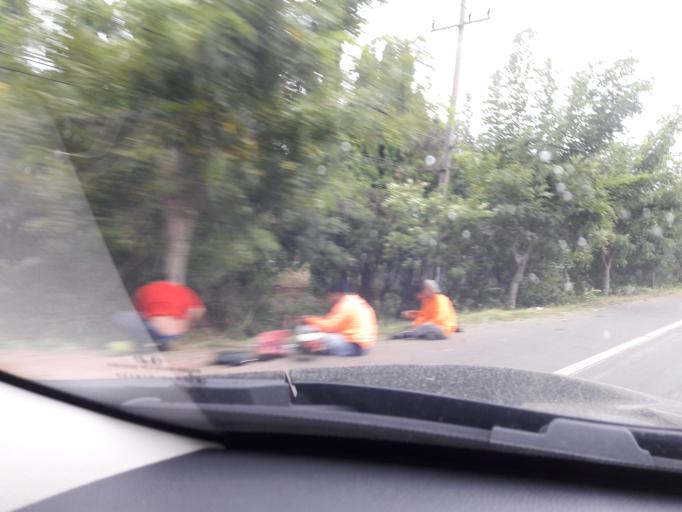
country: TH
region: Ratchaburi
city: Bang Phae
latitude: 13.6356
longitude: 99.9489
